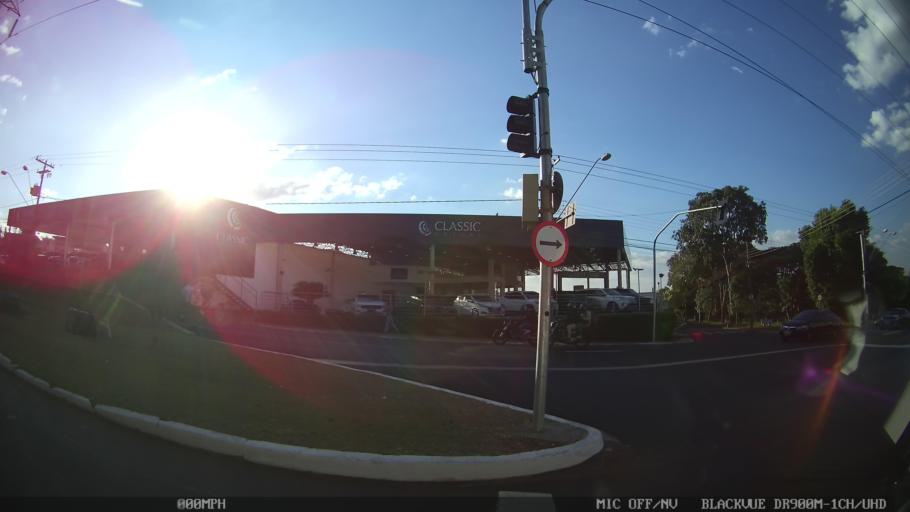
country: BR
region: Sao Paulo
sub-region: Ribeirao Preto
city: Ribeirao Preto
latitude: -21.1959
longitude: -47.8063
